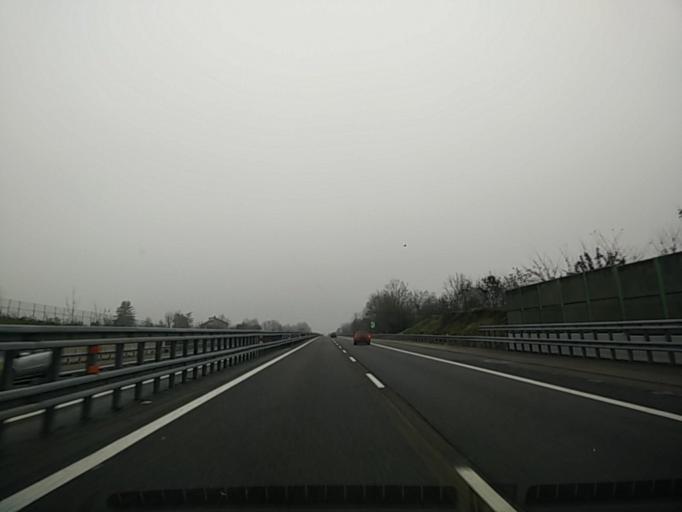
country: IT
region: Piedmont
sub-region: Provincia di Asti
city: Revigliasco d'Asti
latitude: 44.9033
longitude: 8.1493
